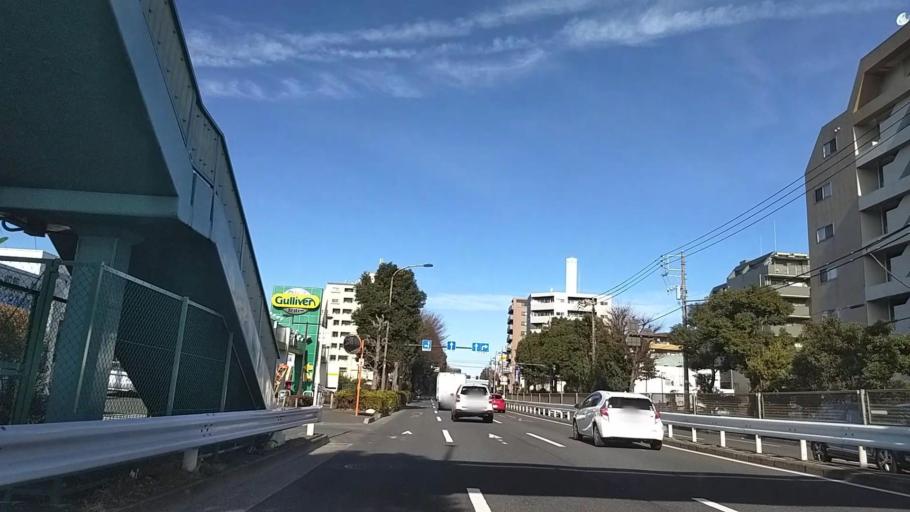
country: JP
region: Tokyo
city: Mitaka-shi
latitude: 35.6542
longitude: 139.6157
